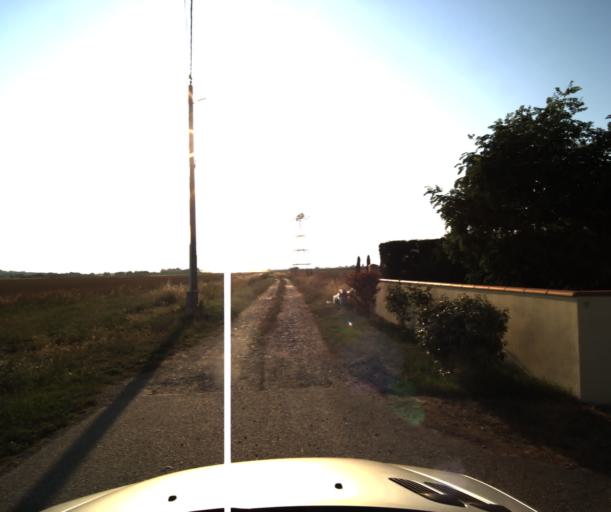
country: FR
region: Midi-Pyrenees
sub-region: Departement de la Haute-Garonne
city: Roquettes
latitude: 43.4810
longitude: 1.3779
